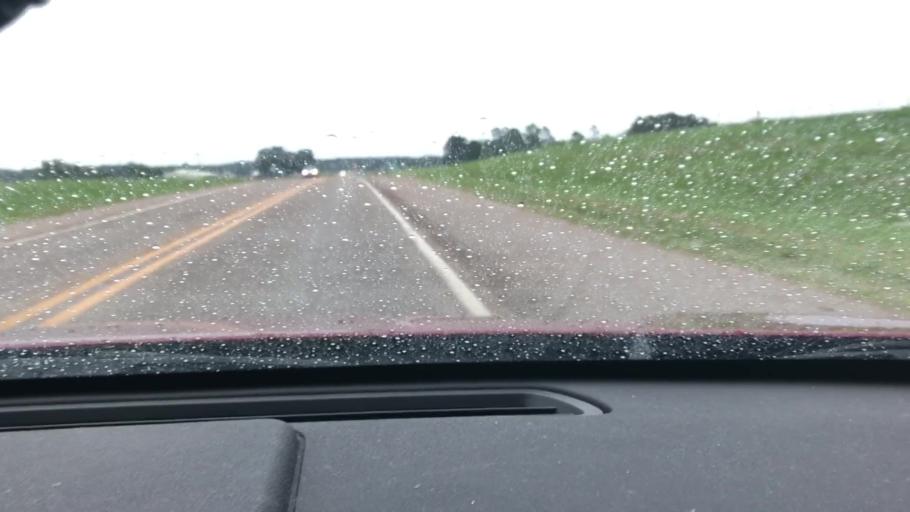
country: US
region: Arkansas
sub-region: Columbia County
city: Magnolia
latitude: 33.2972
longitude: -93.2391
